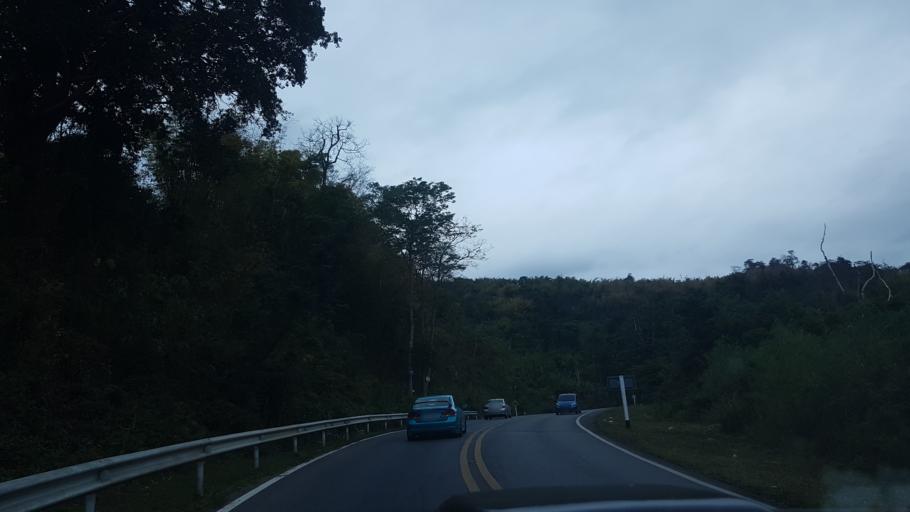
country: TH
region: Phetchabun
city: Khao Kho
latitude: 16.5472
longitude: 101.0353
